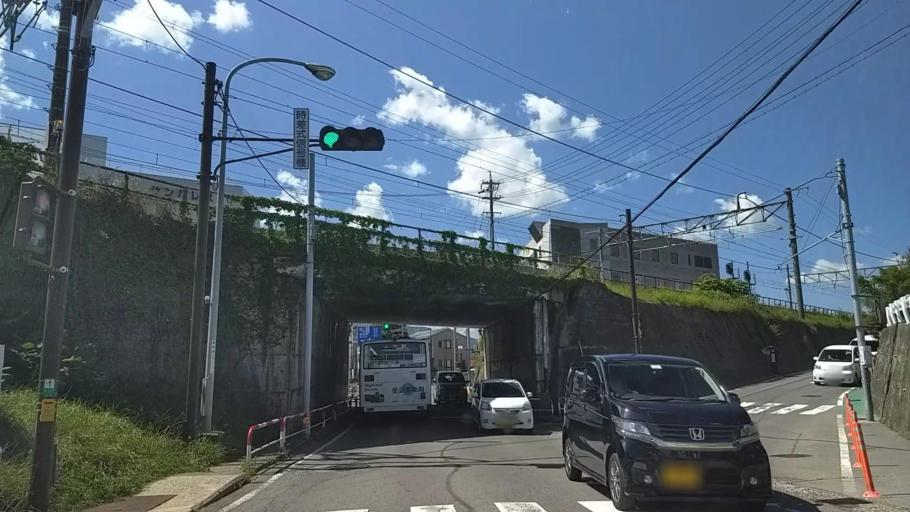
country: JP
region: Nagano
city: Chino
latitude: 35.9964
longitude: 138.1510
